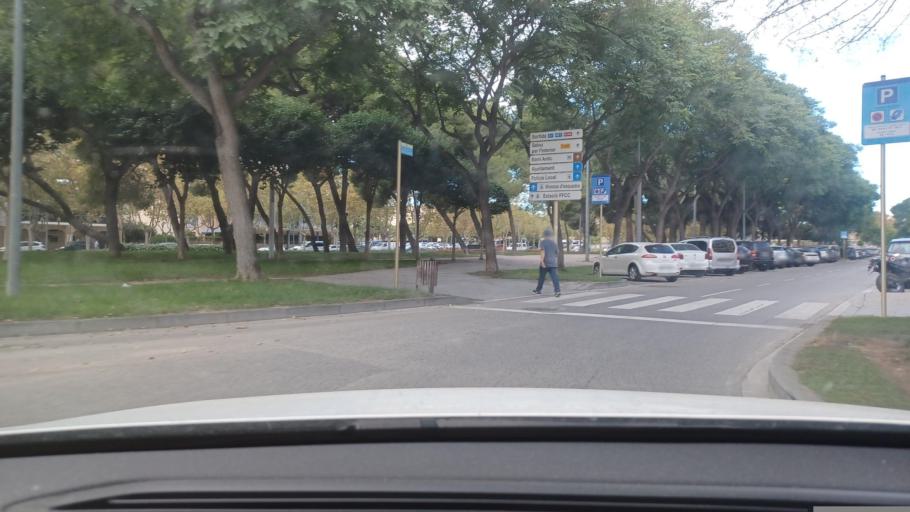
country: ES
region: Catalonia
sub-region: Provincia de Tarragona
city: Cambrils
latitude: 41.0671
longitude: 1.0565
